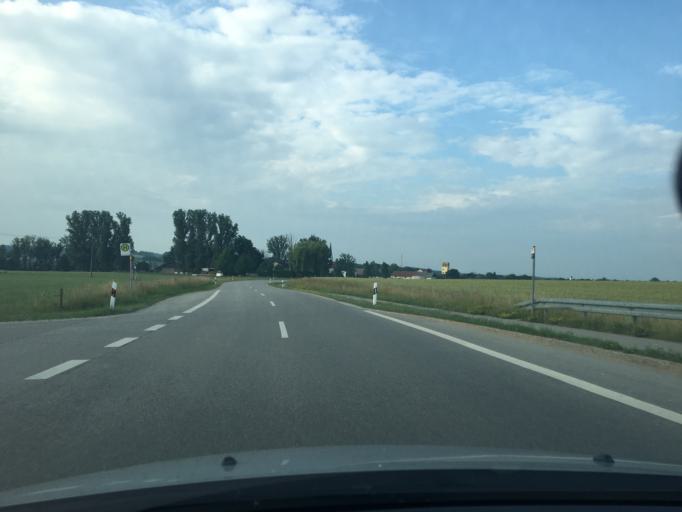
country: DE
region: Bavaria
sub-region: Lower Bavaria
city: Vilsbiburg
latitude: 48.4368
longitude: 12.3438
